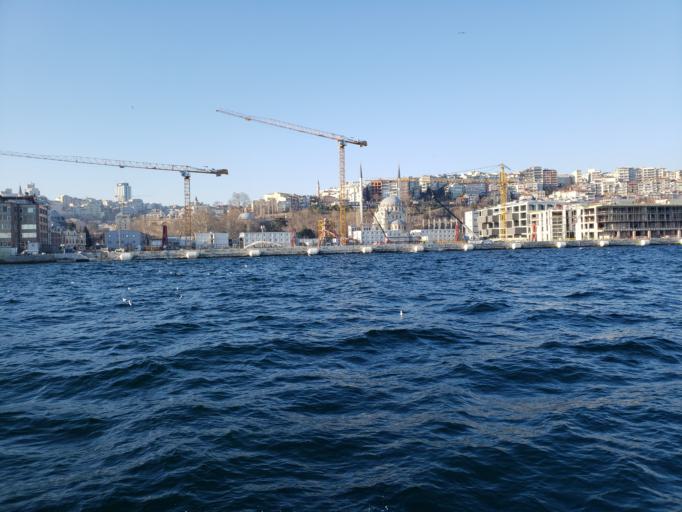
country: TR
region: Istanbul
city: Eminoenue
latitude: 41.0241
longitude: 28.9841
